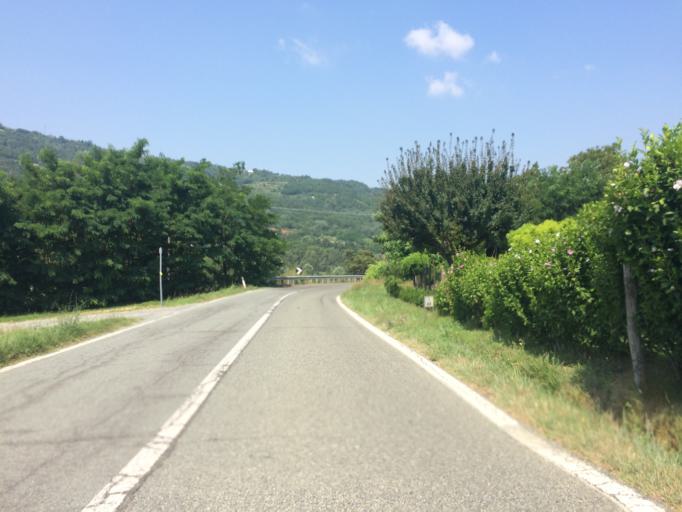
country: IT
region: Piedmont
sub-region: Provincia di Alessandria
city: Melazzo
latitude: 44.6249
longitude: 8.4157
